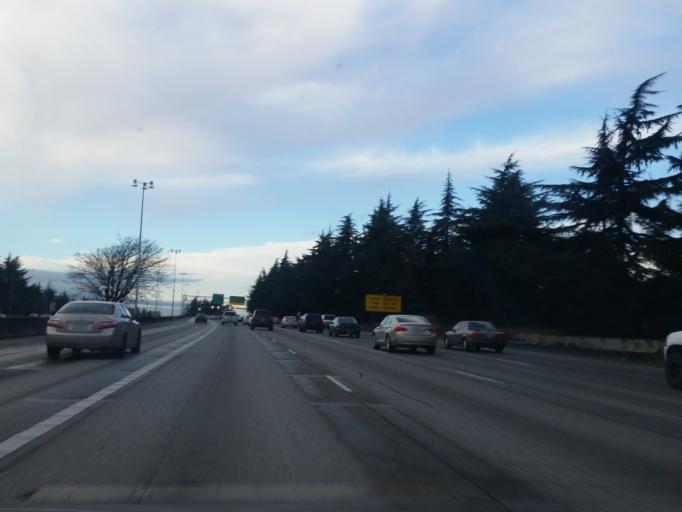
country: US
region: Washington
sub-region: King County
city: White Center
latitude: 47.5544
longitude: -122.3183
